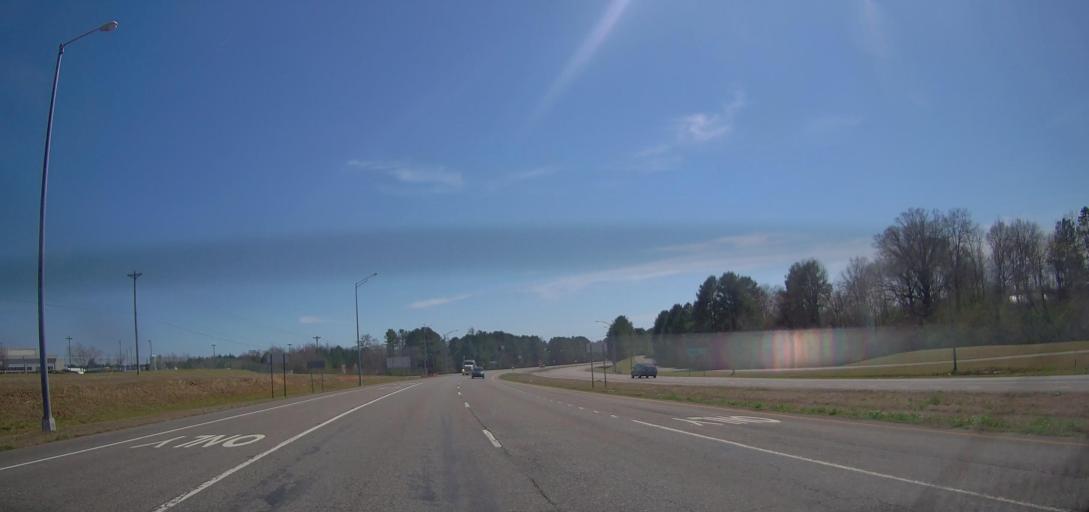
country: US
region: Alabama
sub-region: Cullman County
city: Cullman
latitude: 34.1920
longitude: -86.7859
